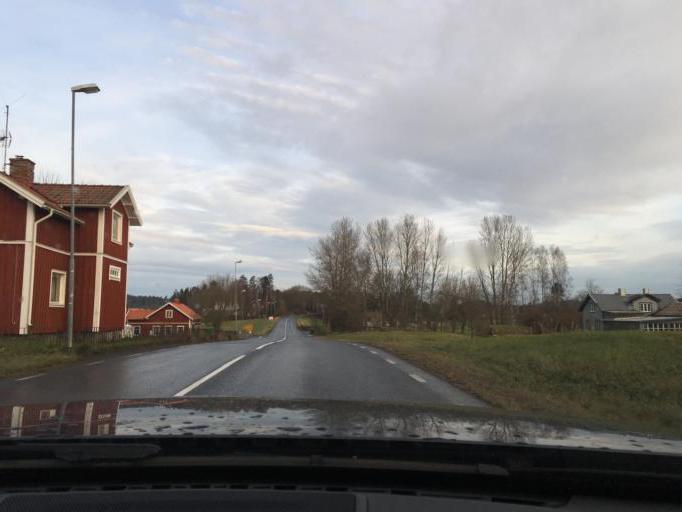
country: SE
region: Joenkoeping
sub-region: Jonkopings Kommun
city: Graenna
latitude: 57.9506
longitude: 14.4146
